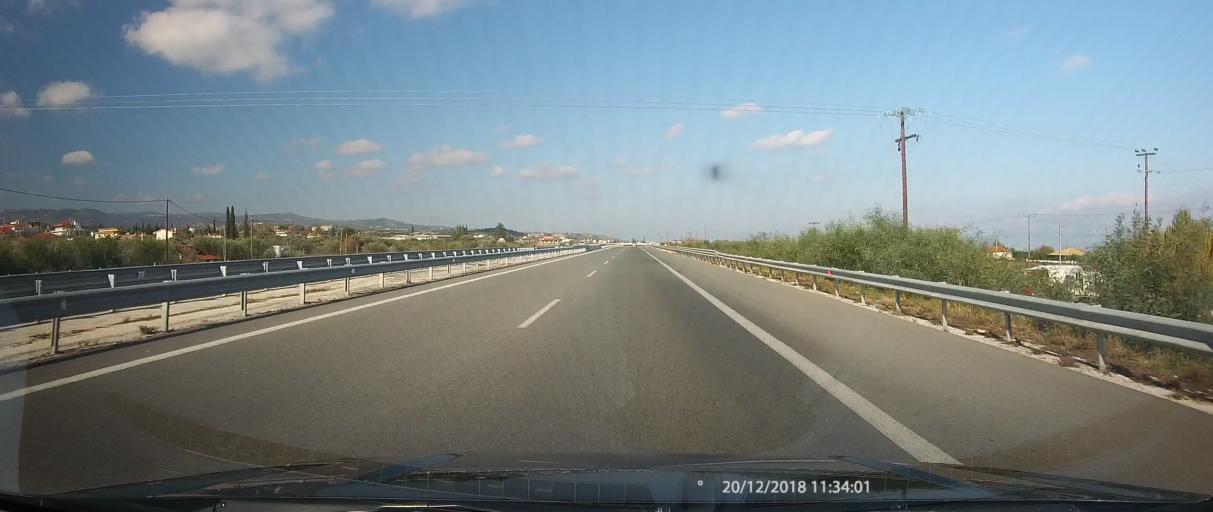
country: GR
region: Peloponnese
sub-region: Nomos Korinthias
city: Velo
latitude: 37.9539
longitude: 22.7532
